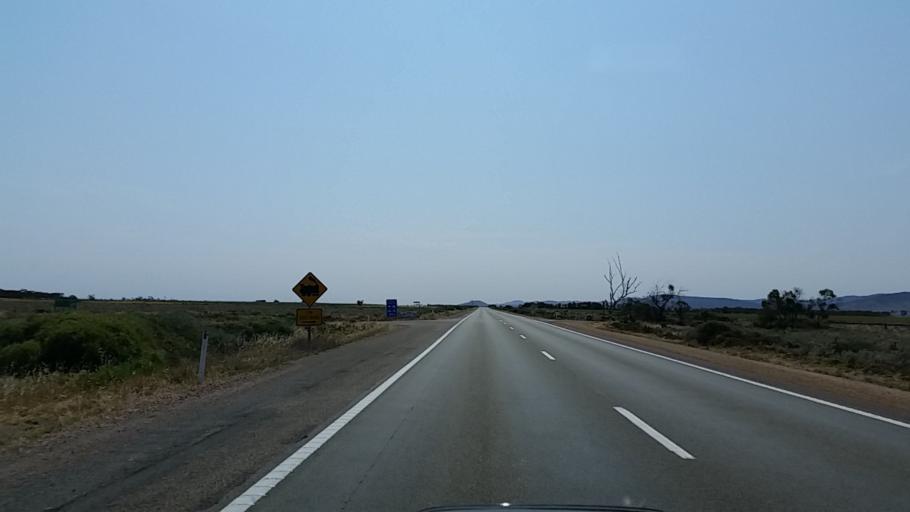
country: AU
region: South Australia
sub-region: Port Pirie City and Dists
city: Port Pirie
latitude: -32.9659
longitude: 137.9825
